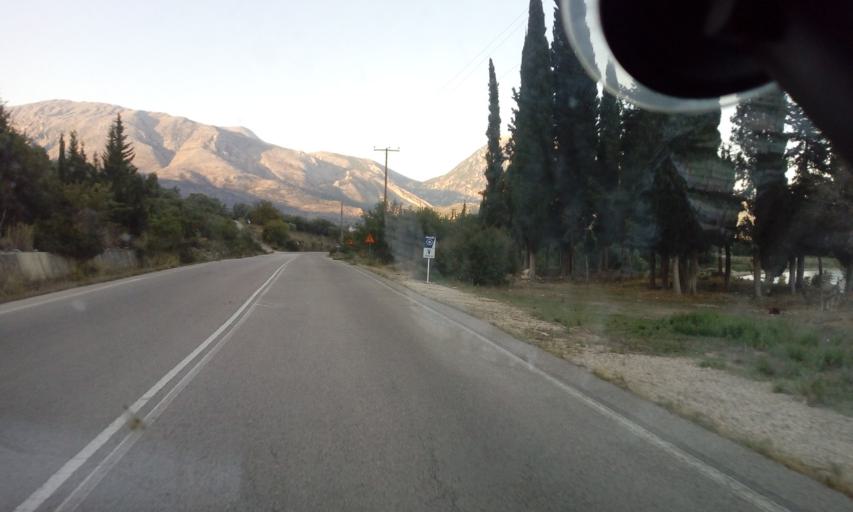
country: GR
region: West Greece
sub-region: Nomos Aitolias kai Akarnanias
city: Kandila
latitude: 38.6769
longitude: 20.9292
